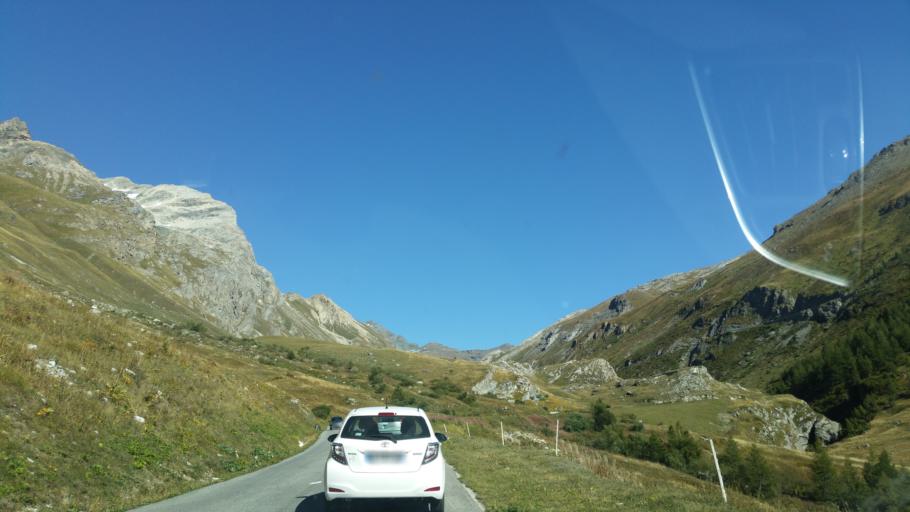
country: FR
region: Rhone-Alpes
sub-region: Departement de la Savoie
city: Val-d'Isere
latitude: 45.4528
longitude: 7.0178
